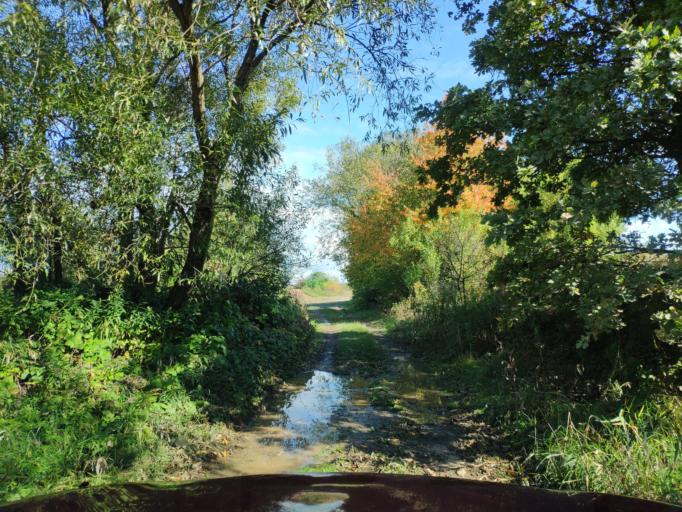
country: SK
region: Presovsky
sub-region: Okres Presov
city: Presov
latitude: 48.9377
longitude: 21.2789
